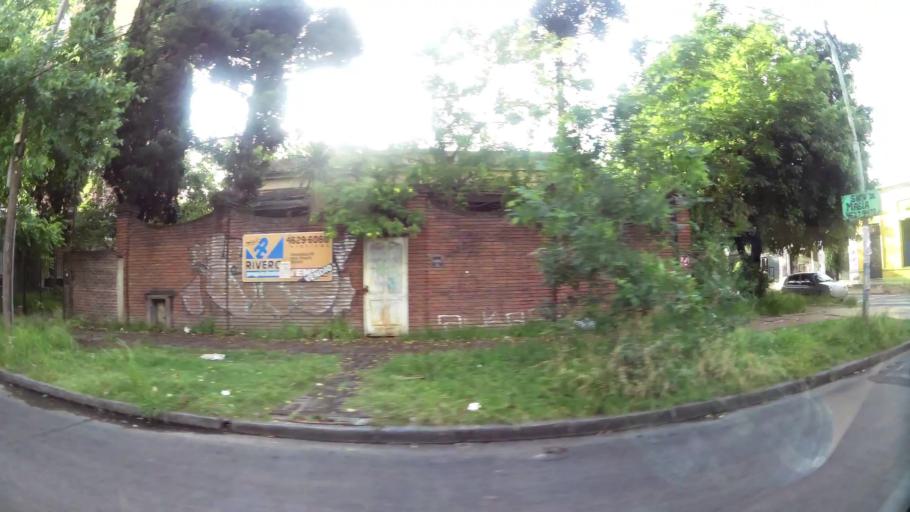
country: AR
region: Buenos Aires
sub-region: Partido de Moron
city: Moron
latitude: -34.6465
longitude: -58.6242
